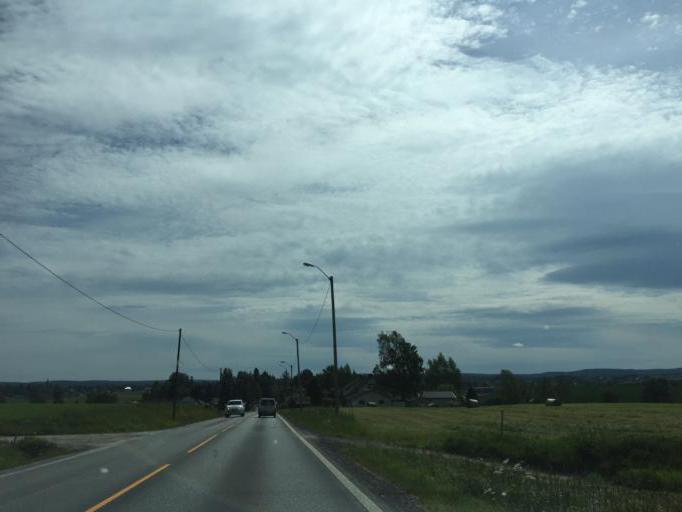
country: NO
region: Akershus
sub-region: Nes
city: Arnes
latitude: 60.1288
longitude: 11.4441
